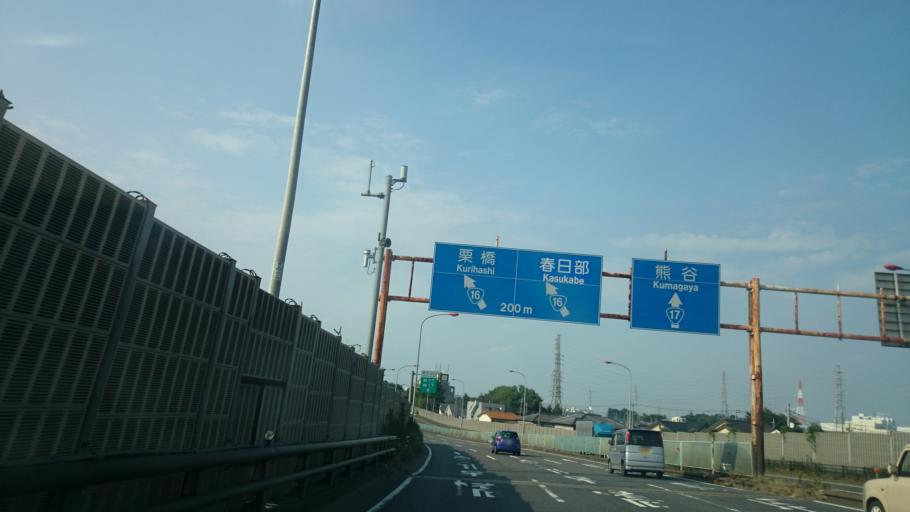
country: JP
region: Saitama
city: Ageoshimo
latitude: 35.9472
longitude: 139.6079
